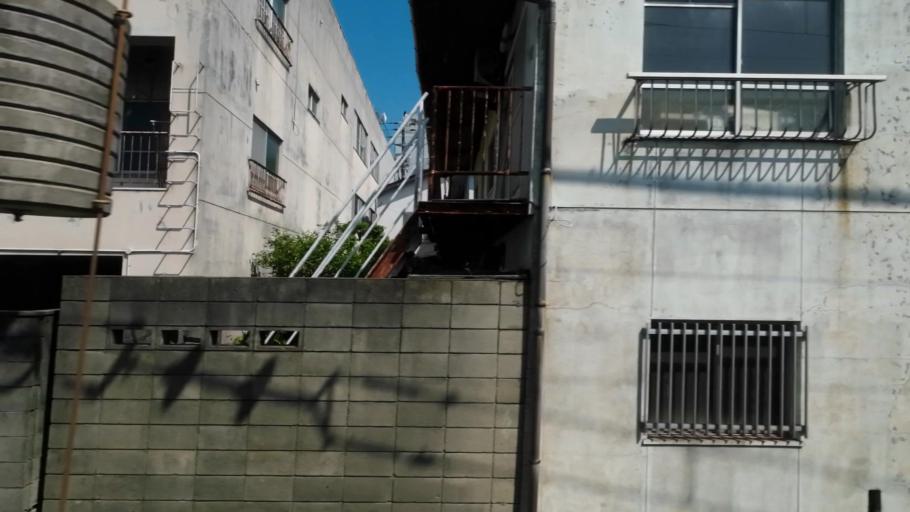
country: JP
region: Kagawa
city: Kan'onjicho
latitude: 34.1237
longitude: 133.6536
